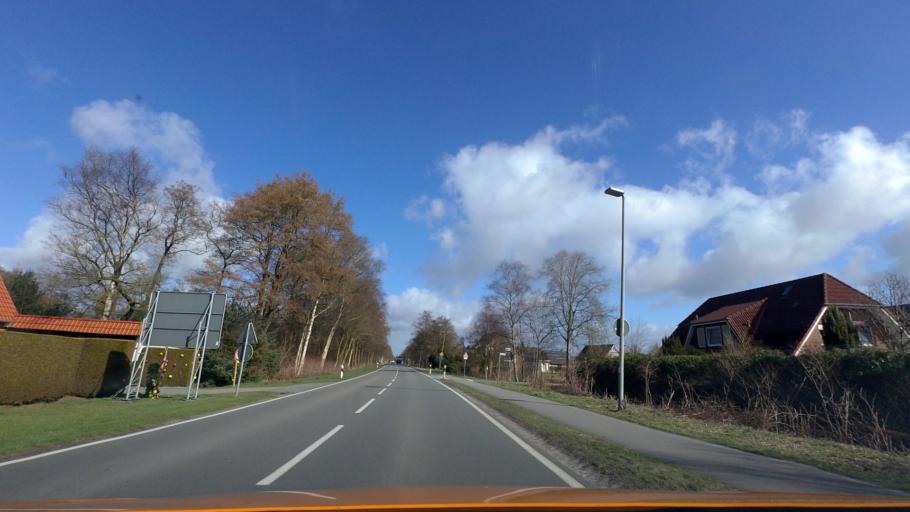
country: DE
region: Lower Saxony
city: Edewecht
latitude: 53.0888
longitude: 7.9409
